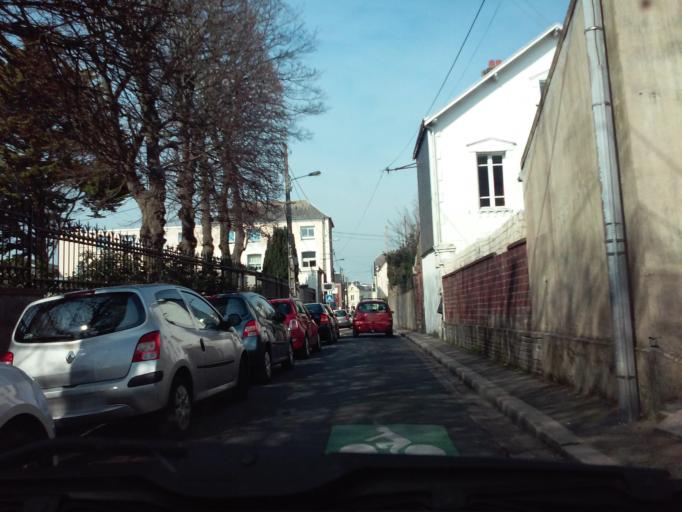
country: FR
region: Haute-Normandie
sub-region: Departement de la Seine-Maritime
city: Le Havre
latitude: 49.5073
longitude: 0.1076
